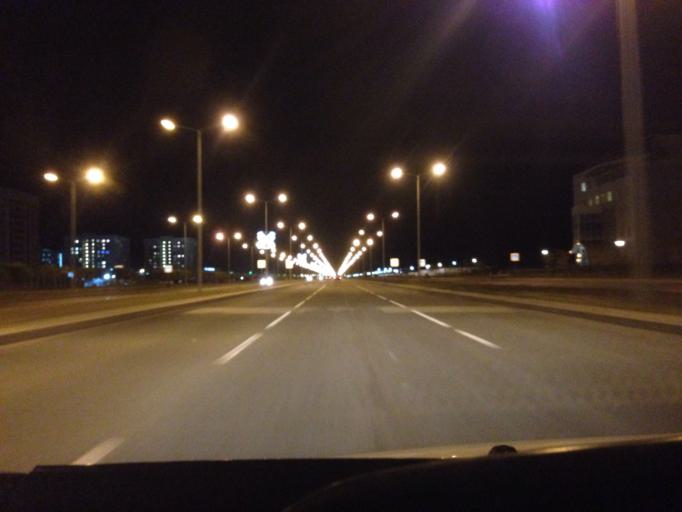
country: KZ
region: Astana Qalasy
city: Astana
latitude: 51.0954
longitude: 71.3932
